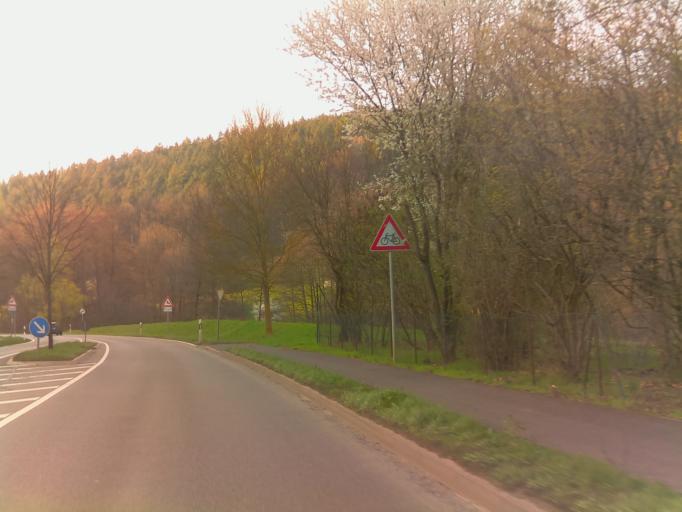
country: DE
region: Thuringia
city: Unterbreizbach
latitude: 50.8578
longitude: 9.9454
